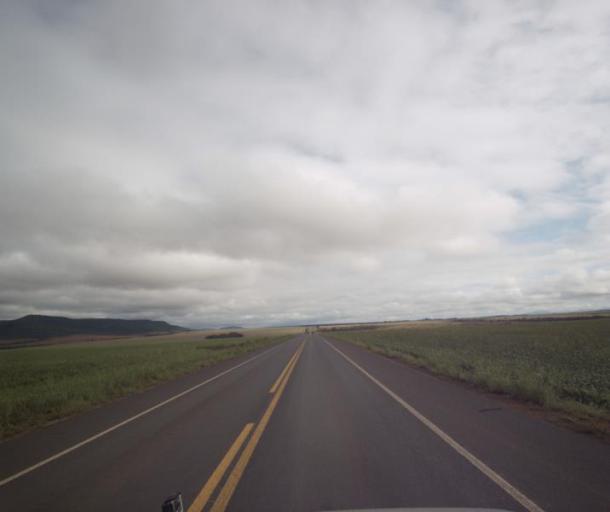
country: BR
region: Goias
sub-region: Padre Bernardo
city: Padre Bernardo
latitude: -15.4064
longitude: -48.6298
